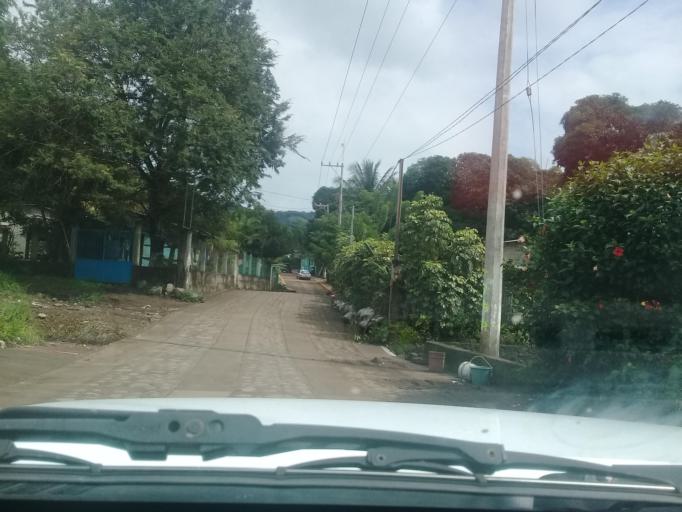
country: MX
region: Veracruz
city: Comoapan
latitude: 18.4095
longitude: -95.1594
